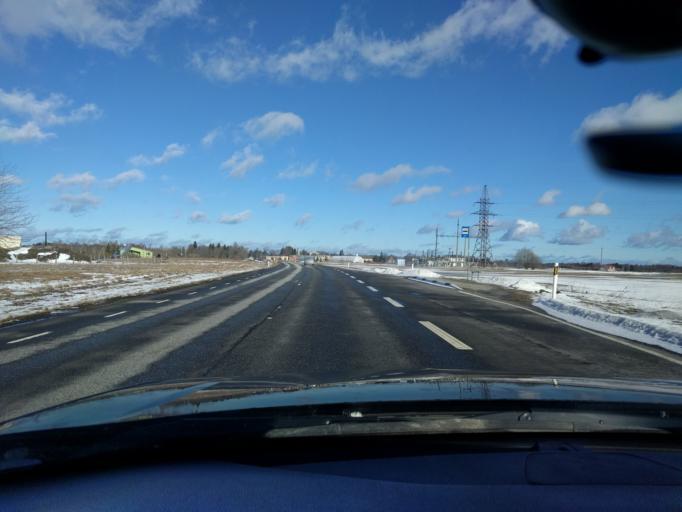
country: EE
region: Harju
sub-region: Raasiku vald
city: Raasiku
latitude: 59.3704
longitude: 25.1926
